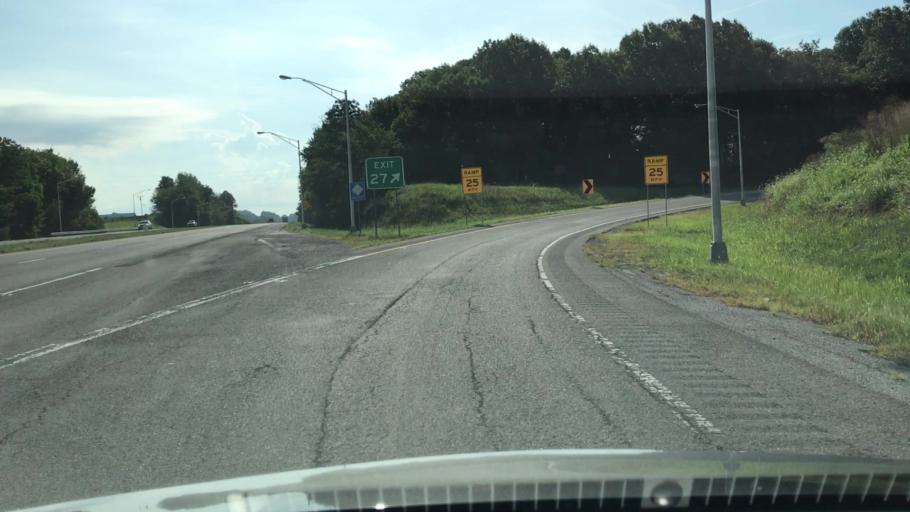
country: US
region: Kentucky
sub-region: Metcalfe County
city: Edmonton
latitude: 36.9963
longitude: -85.6576
